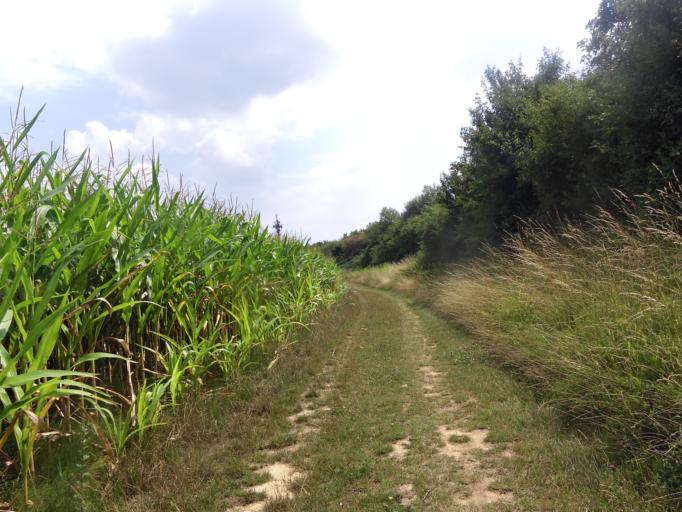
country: DE
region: Bavaria
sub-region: Regierungsbezirk Unterfranken
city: Randersacker
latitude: 49.7362
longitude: 9.9692
